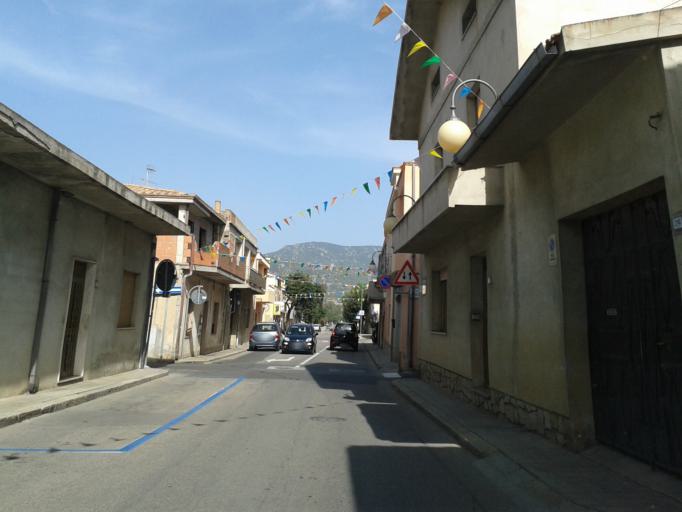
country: IT
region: Sardinia
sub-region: Provincia di Cagliari
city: Villasimius
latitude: 39.1457
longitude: 9.5170
